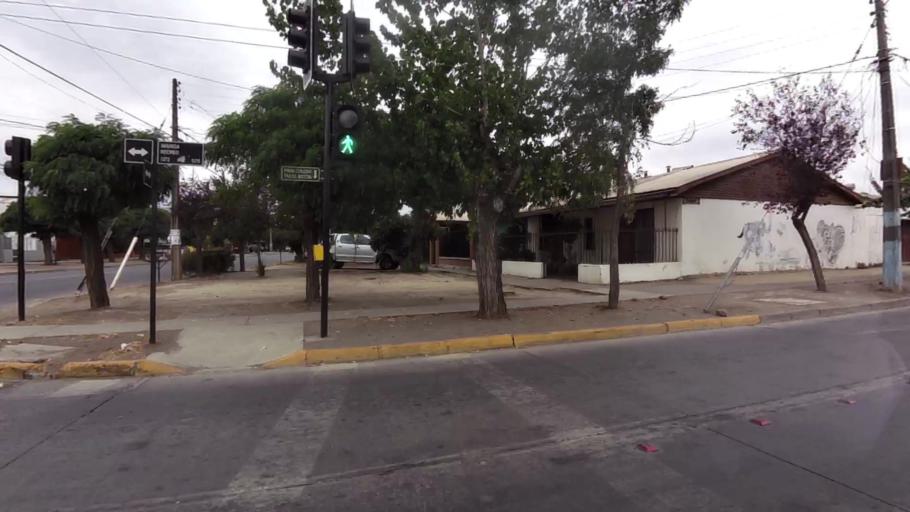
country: CL
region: O'Higgins
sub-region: Provincia de Cachapoal
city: Rancagua
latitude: -34.1504
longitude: -70.7368
